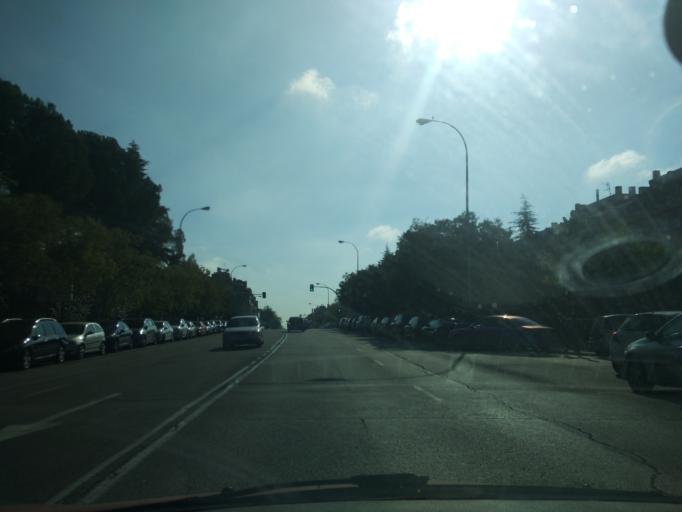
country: ES
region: Madrid
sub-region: Provincia de Madrid
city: Fuencarral-El Pardo
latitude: 40.4899
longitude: -3.7163
